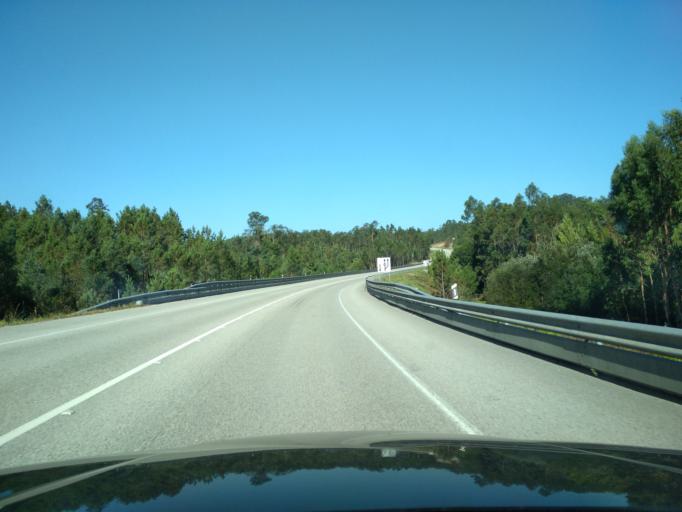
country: PT
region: Leiria
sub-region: Pombal
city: Lourical
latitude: 39.9856
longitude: -8.7631
